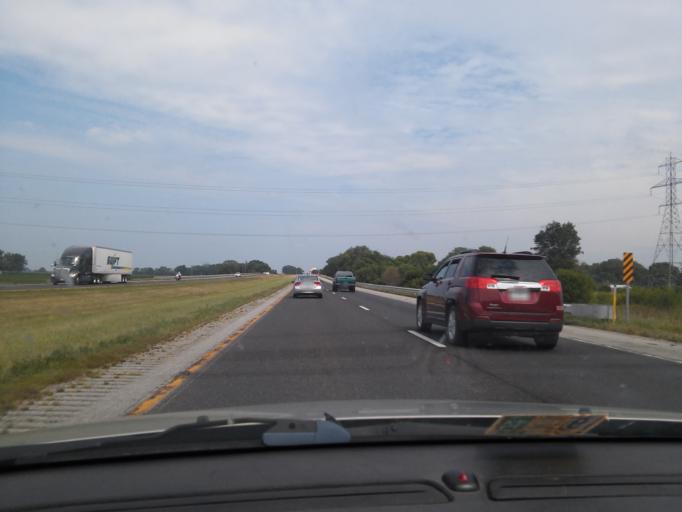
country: US
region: Indiana
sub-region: Wayne County
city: Cambridge City
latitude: 39.8532
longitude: -85.1116
